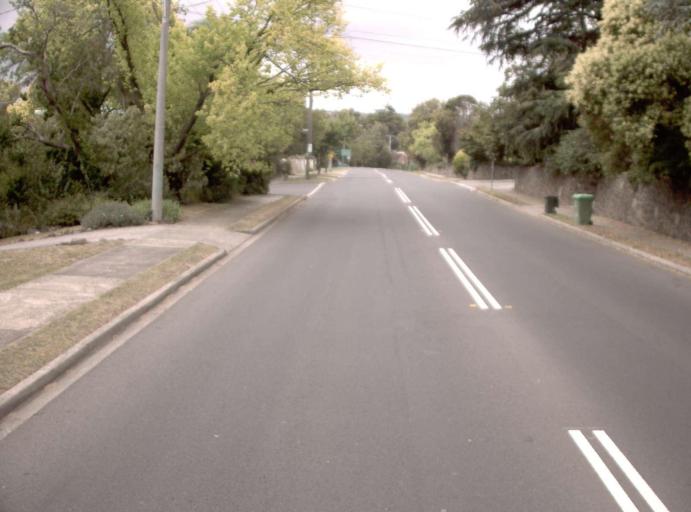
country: AU
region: Victoria
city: Ivanhoe East
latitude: -37.7745
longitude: 145.0647
